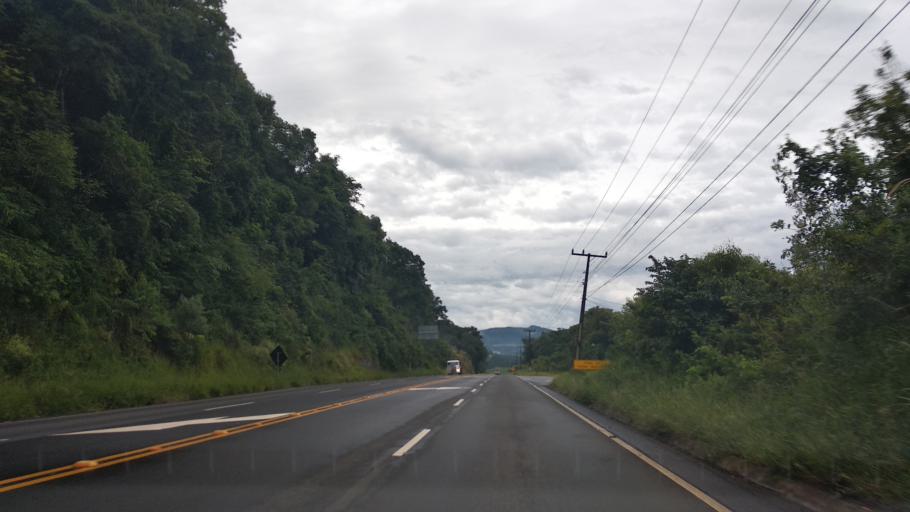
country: BR
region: Santa Catarina
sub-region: Videira
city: Videira
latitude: -27.0633
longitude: -51.2316
